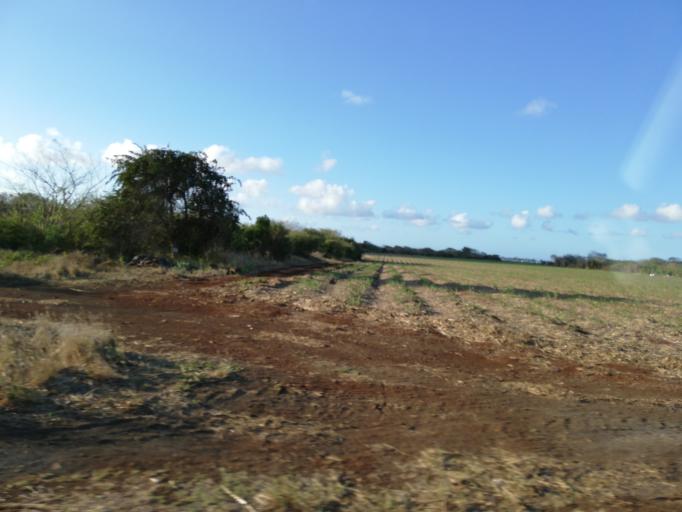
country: MU
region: Pamplemousses
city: Grande Pointe aux Piments
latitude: -20.0723
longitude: 57.5255
